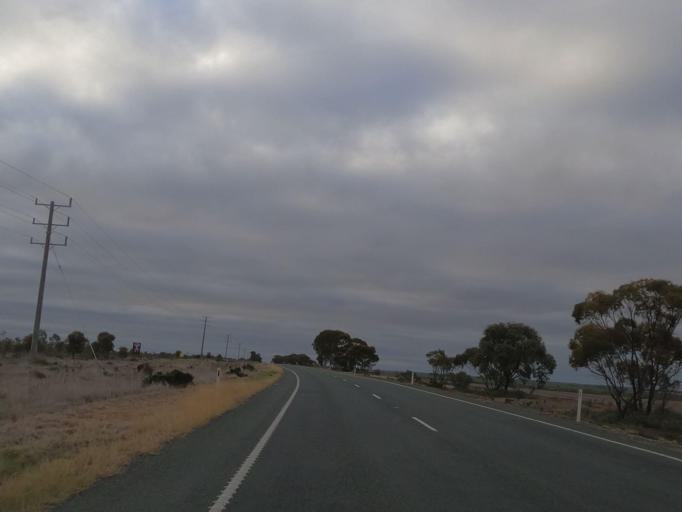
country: AU
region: Victoria
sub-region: Swan Hill
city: Swan Hill
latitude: -35.5757
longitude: 143.7878
